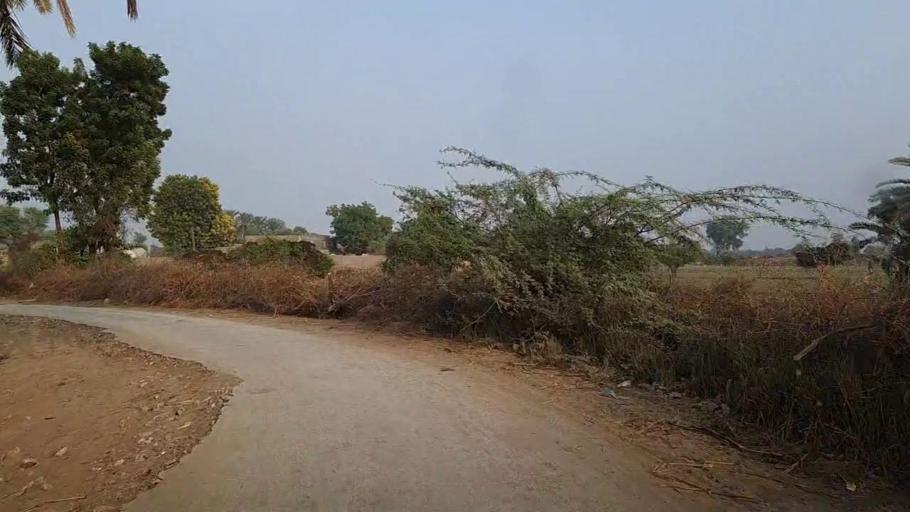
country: PK
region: Sindh
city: Setharja Old
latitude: 27.0986
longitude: 68.5041
